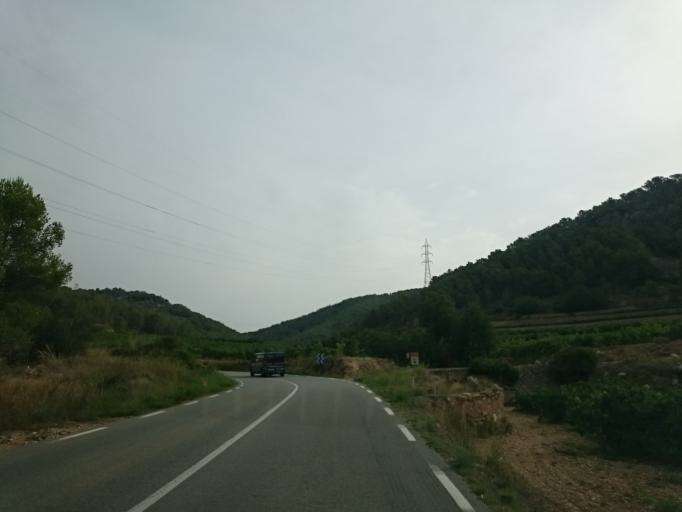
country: ES
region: Catalonia
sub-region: Provincia de Barcelona
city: Sant Pere de Ribes
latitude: 41.2744
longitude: 1.7882
